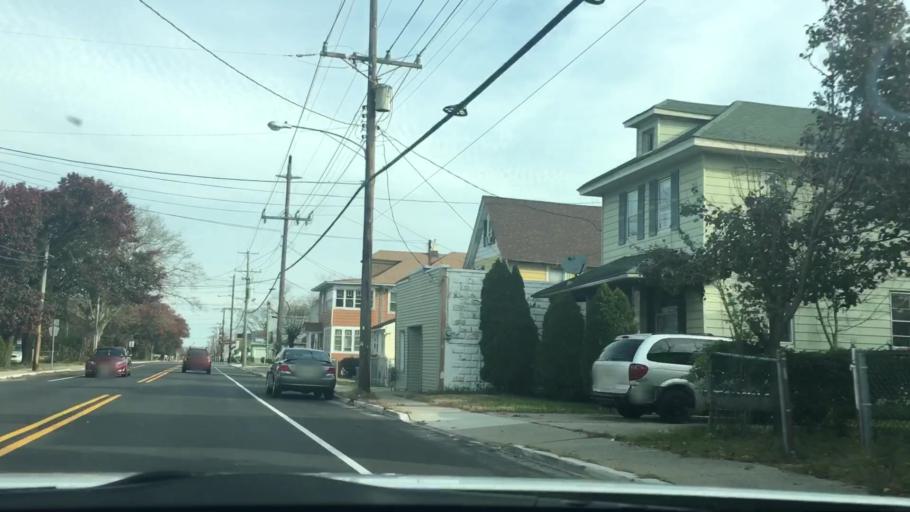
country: US
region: New Jersey
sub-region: Atlantic County
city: Pleasantville
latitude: 39.3949
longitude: -74.5286
